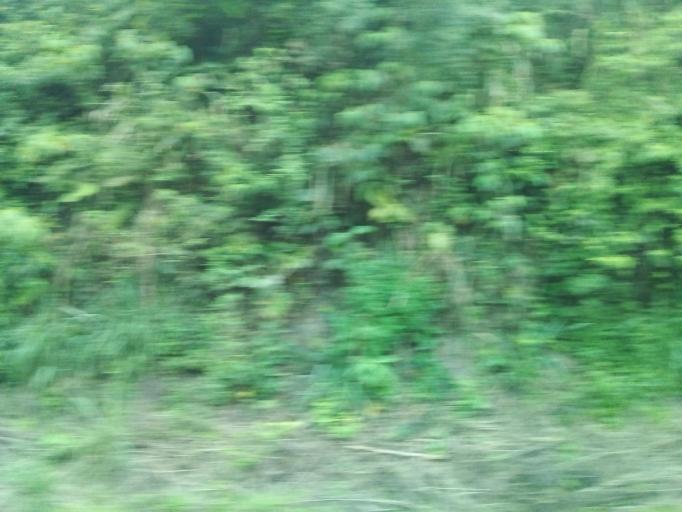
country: BR
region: Minas Gerais
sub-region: Joao Monlevade
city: Joao Monlevade
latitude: -19.8254
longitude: -43.1231
